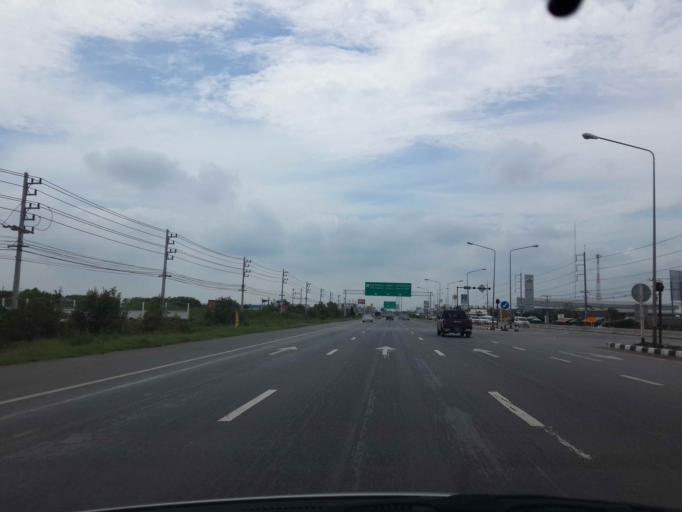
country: TH
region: Samut Songkhram
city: Samut Songkhram
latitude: 13.4091
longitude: 100.0202
